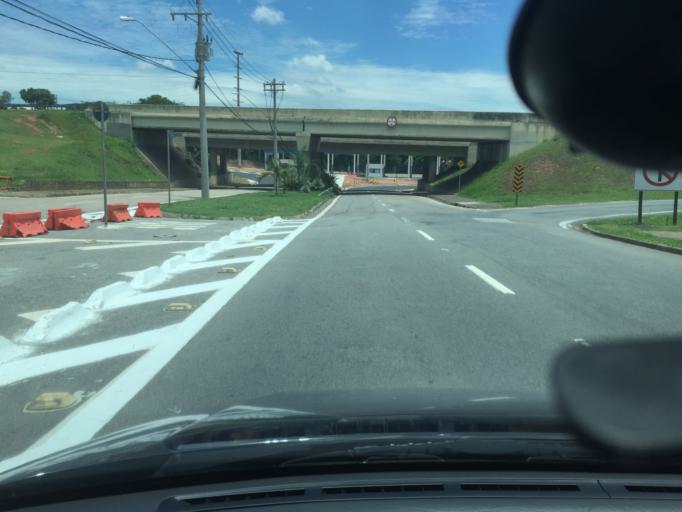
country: BR
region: Sao Paulo
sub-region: Jundiai
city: Jundiai
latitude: -23.1609
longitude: -46.9006
